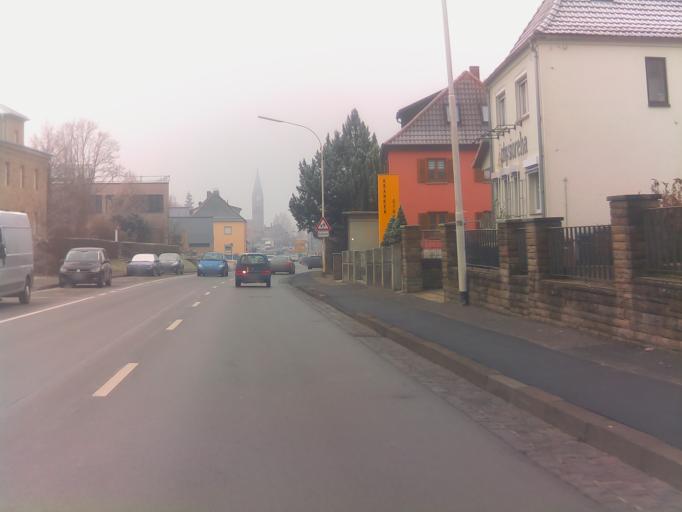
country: DE
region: Bavaria
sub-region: Regierungsbezirk Unterfranken
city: Hassfurt
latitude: 50.0364
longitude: 10.5149
